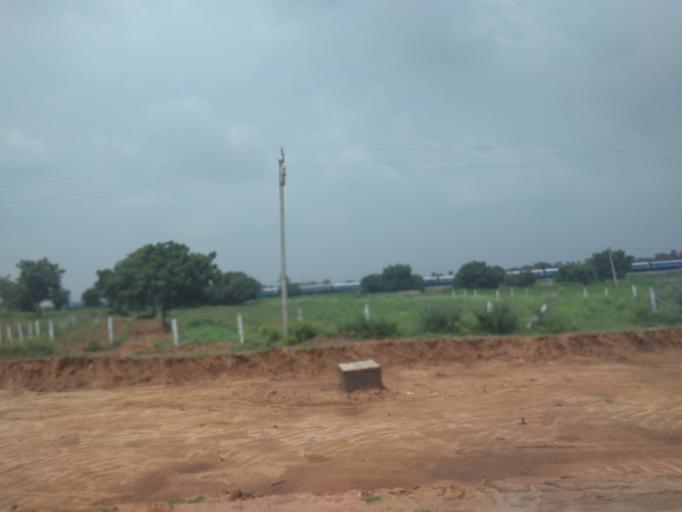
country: IN
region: Telangana
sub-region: Warangal
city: Jangaon
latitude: 17.6645
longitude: 79.0847
